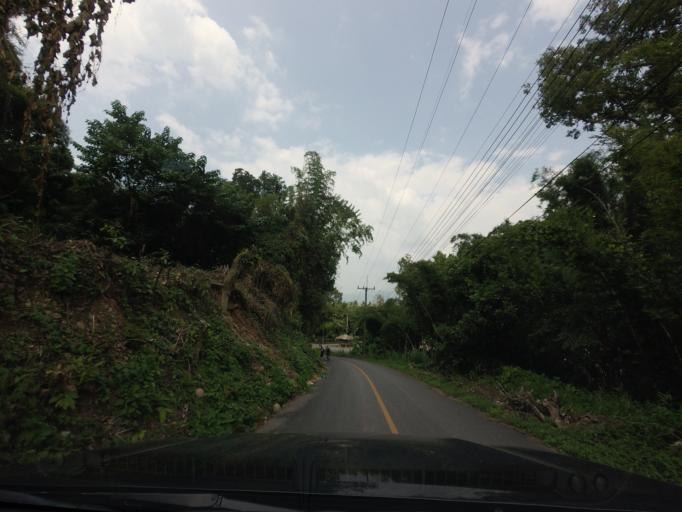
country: TH
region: Nan
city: Pua
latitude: 19.1696
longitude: 100.9273
